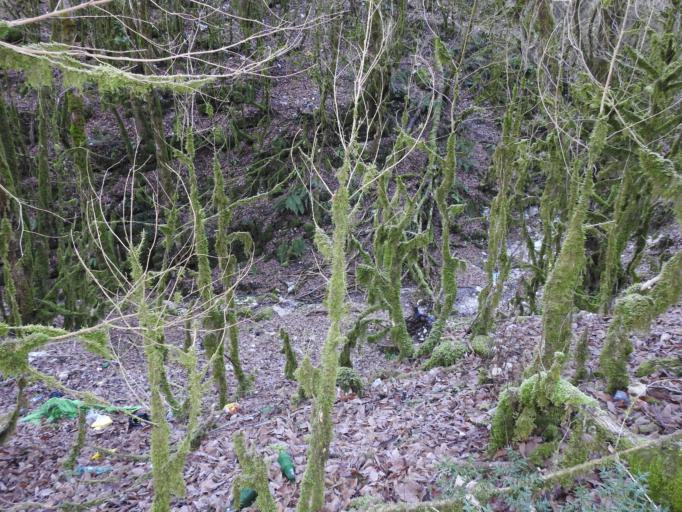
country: GE
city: Gantiadi
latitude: 43.4191
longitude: 40.1150
